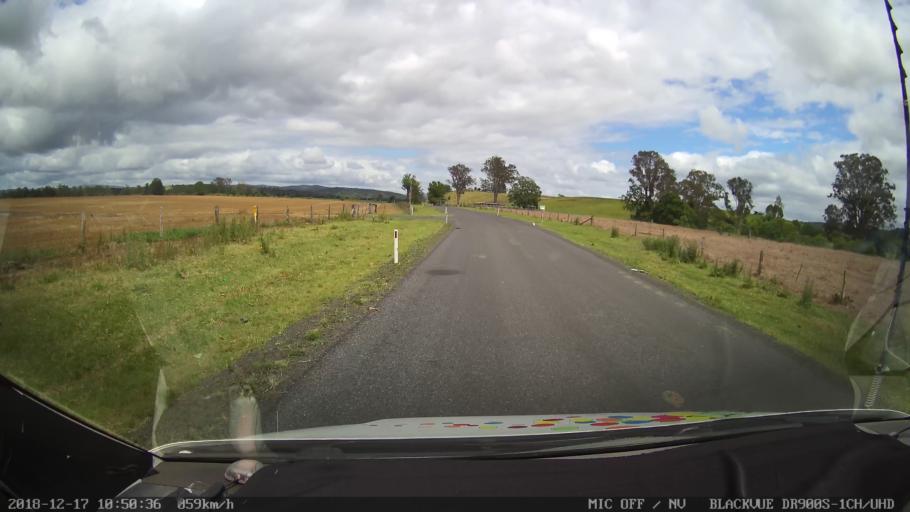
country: AU
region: New South Wales
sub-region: Clarence Valley
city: Gordon
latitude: -28.8582
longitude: 152.5733
